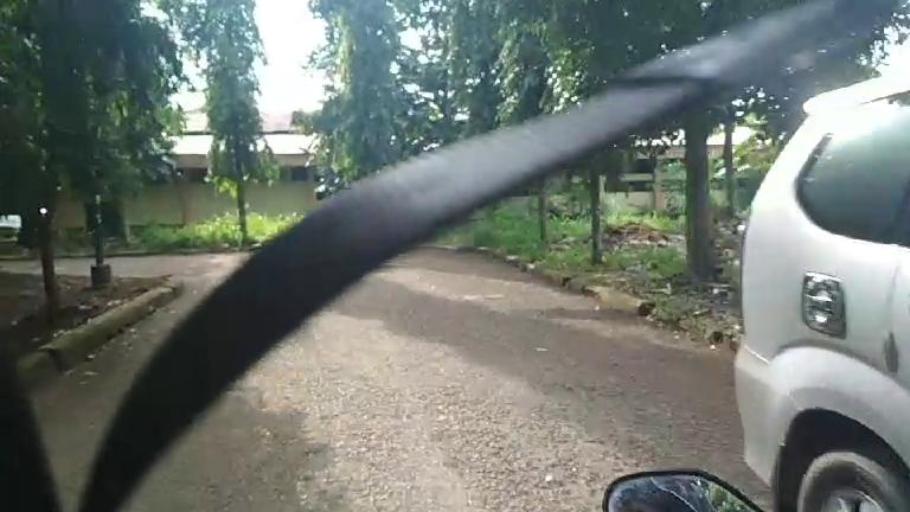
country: ID
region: South Sulawesi
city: Makassar
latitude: -5.1286
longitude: 119.4807
